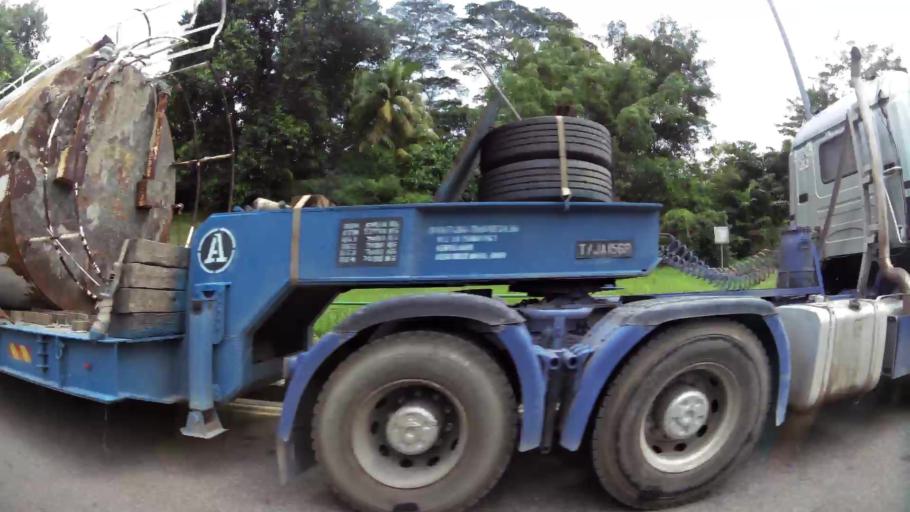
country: MY
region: Johor
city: Johor Bahru
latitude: 1.4340
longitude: 103.7622
